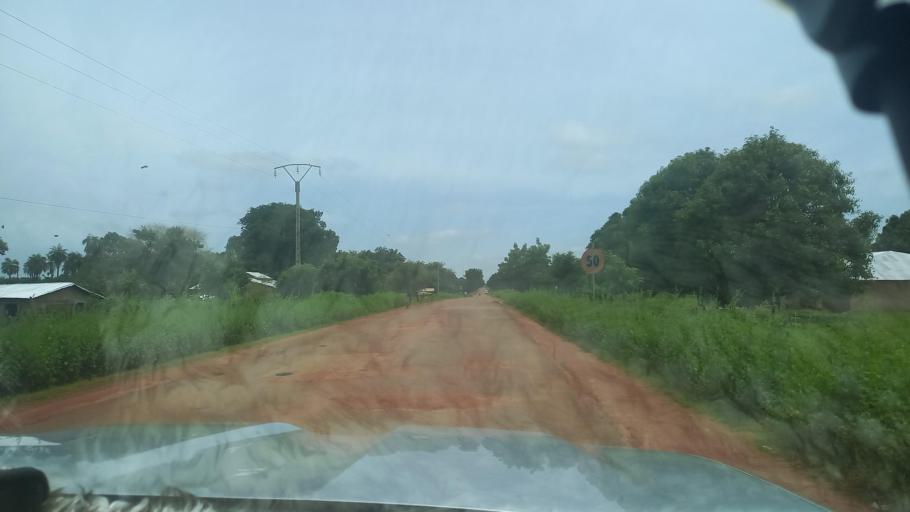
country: SN
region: Kolda
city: Marsassoum
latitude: 12.9665
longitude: -15.9626
